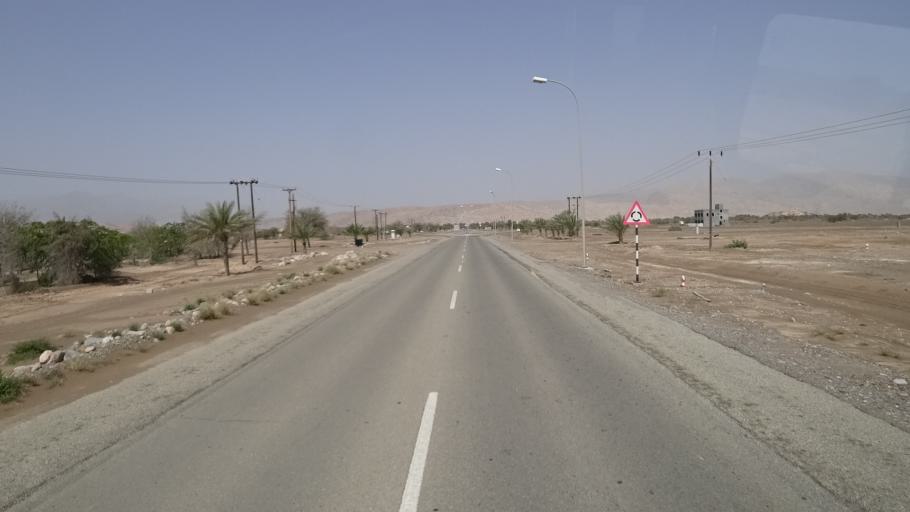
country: OM
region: Muhafazat Masqat
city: Muscat
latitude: 23.2167
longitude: 58.9275
